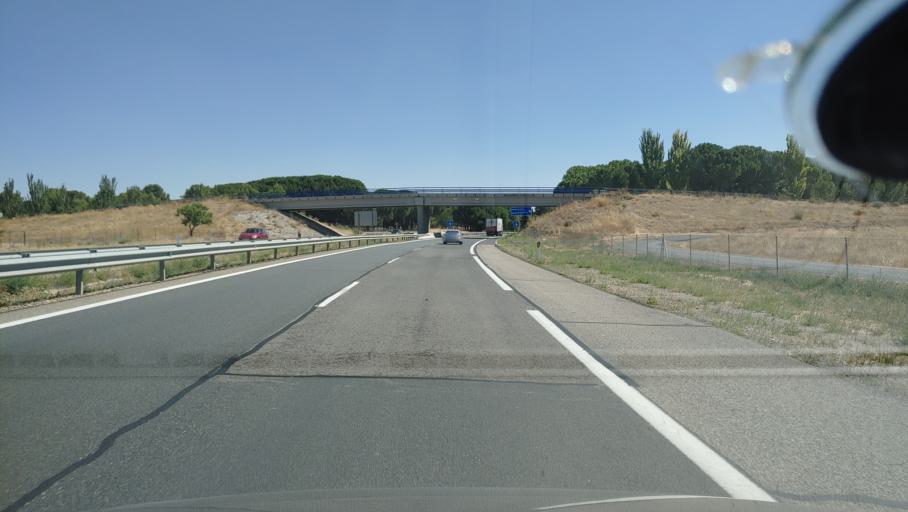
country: ES
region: Castille-La Mancha
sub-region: Provincia de Ciudad Real
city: Villarta de San Juan
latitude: 39.2439
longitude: -3.4165
